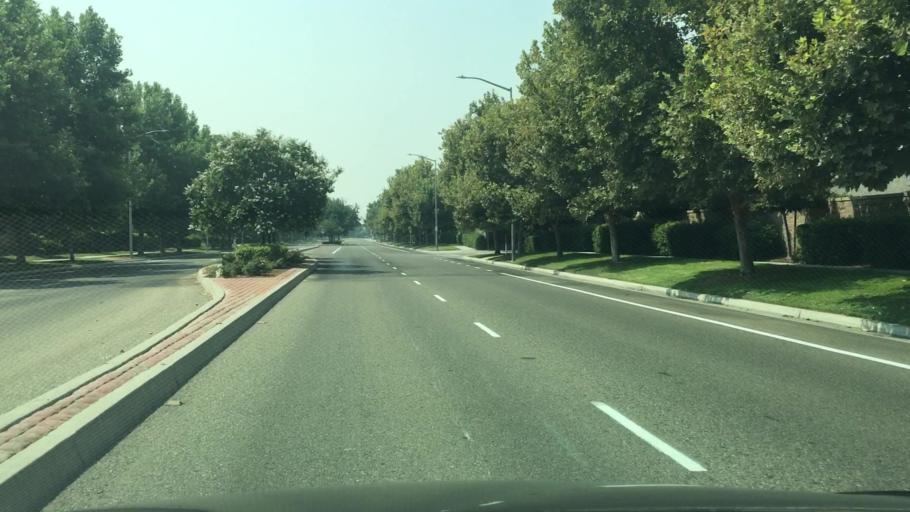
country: US
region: California
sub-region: Fresno County
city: Clovis
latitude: 36.8644
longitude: -119.7022
